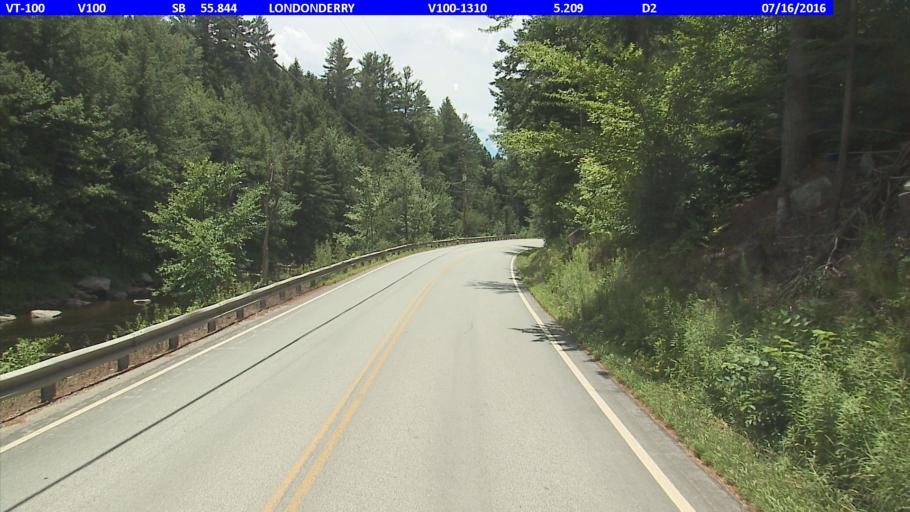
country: US
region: Vermont
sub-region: Windsor County
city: Chester
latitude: 43.2217
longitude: -72.8201
